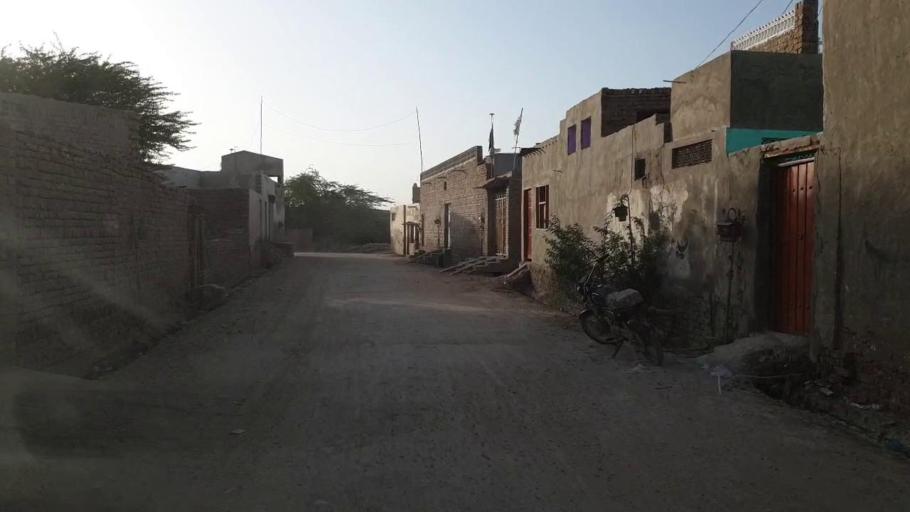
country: PK
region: Sindh
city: Jam Sahib
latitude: 26.2936
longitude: 68.6277
